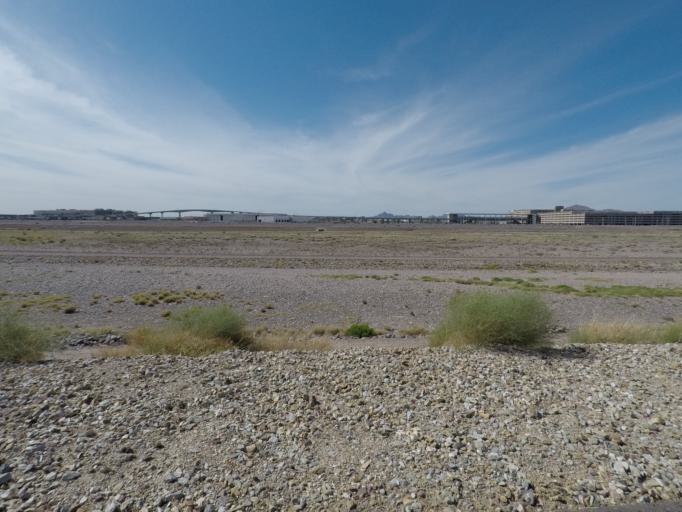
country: US
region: Arizona
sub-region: Maricopa County
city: Tempe Junction
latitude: 33.4288
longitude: -111.9853
